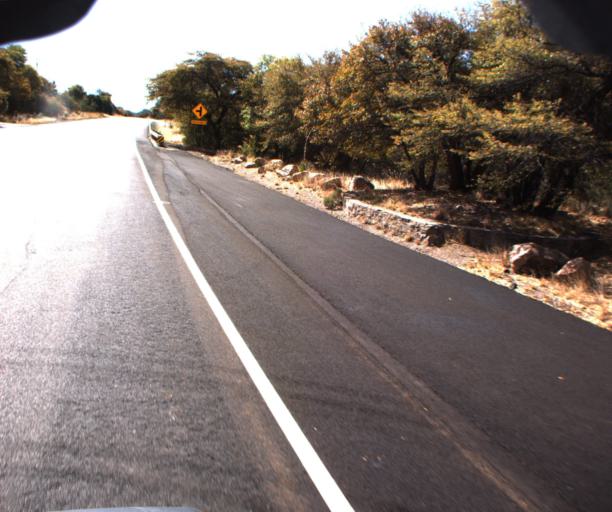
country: US
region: Arizona
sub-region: Cochise County
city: Bisbee
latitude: 31.4644
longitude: -109.9504
